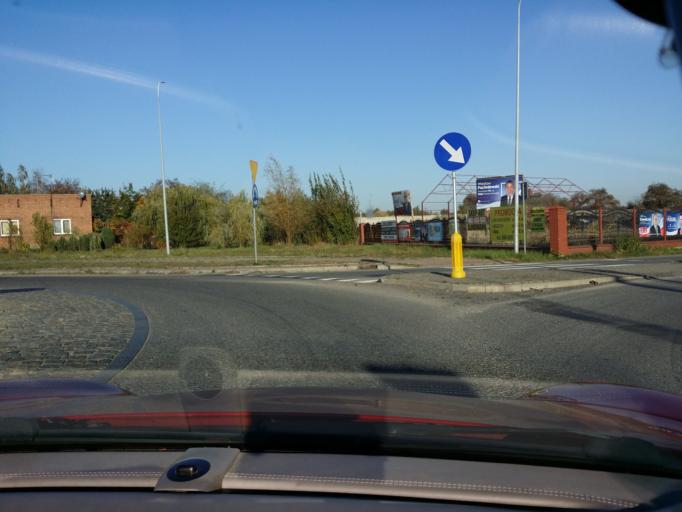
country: PL
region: Masovian Voivodeship
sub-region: Powiat radomski
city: Trablice
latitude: 51.3218
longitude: 21.1216
